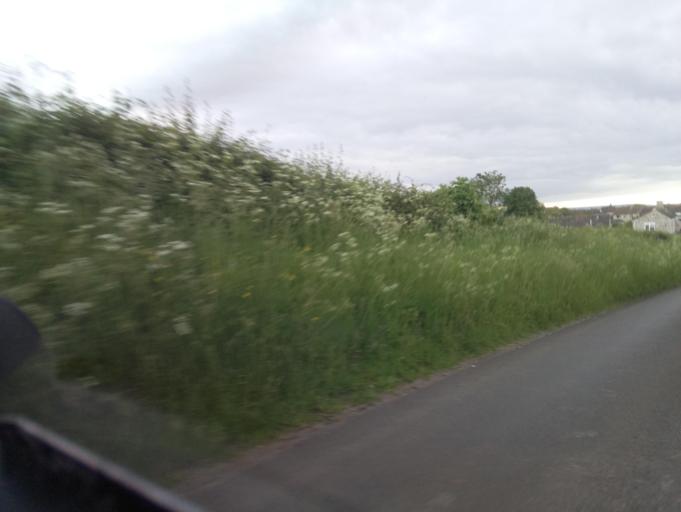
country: GB
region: England
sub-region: South Gloucestershire
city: Pucklechurch
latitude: 51.4600
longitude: -2.4256
